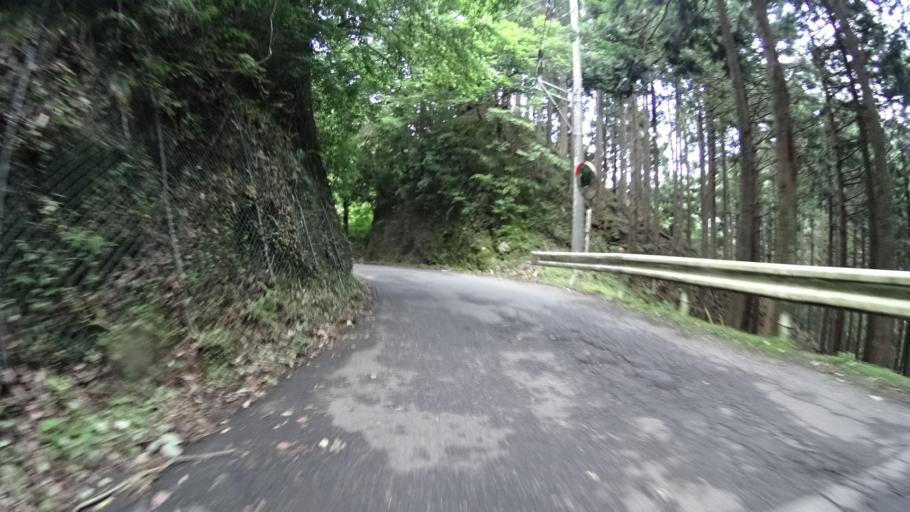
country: JP
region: Kanagawa
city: Hadano
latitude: 35.4986
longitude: 139.2261
